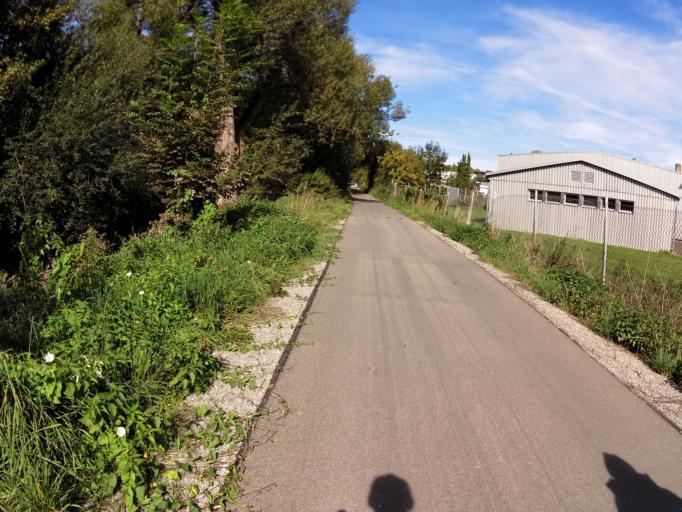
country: DE
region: Baden-Wuerttemberg
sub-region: Freiburg Region
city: Dauchingen
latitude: 48.0612
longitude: 8.5594
